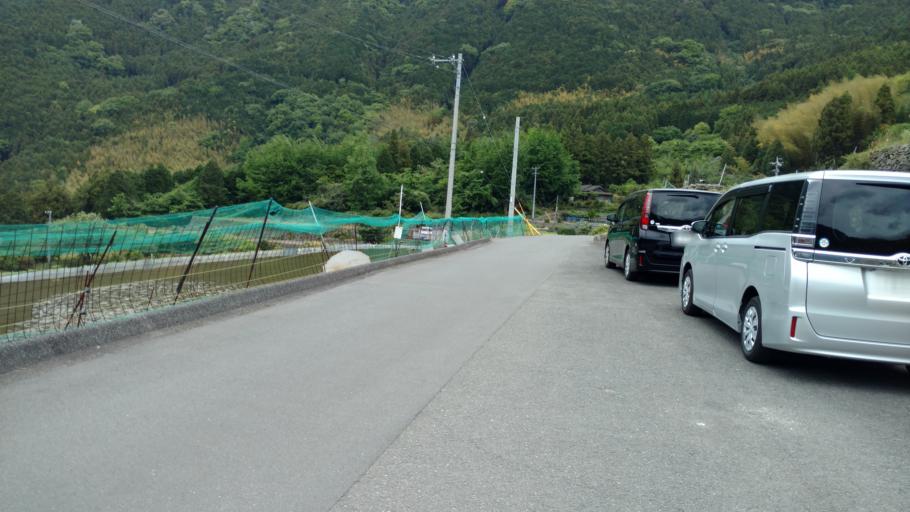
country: JP
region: Ehime
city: Saijo
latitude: 33.8635
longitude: 133.1977
